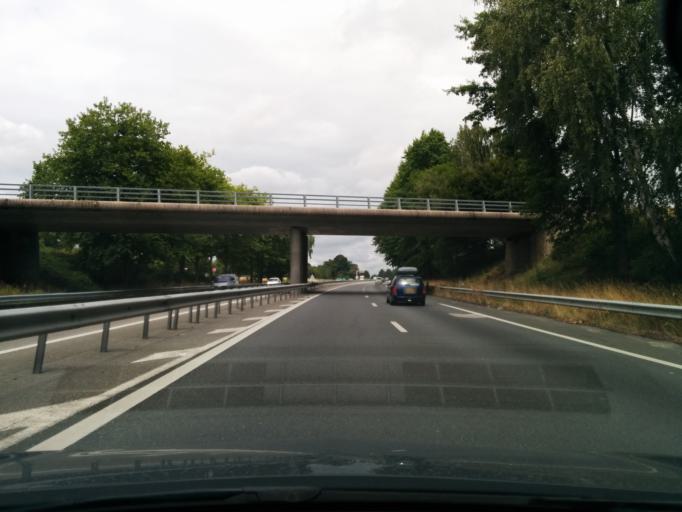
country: FR
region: Limousin
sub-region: Departement de la Haute-Vienne
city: Boisseuil
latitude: 45.7548
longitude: 1.3329
